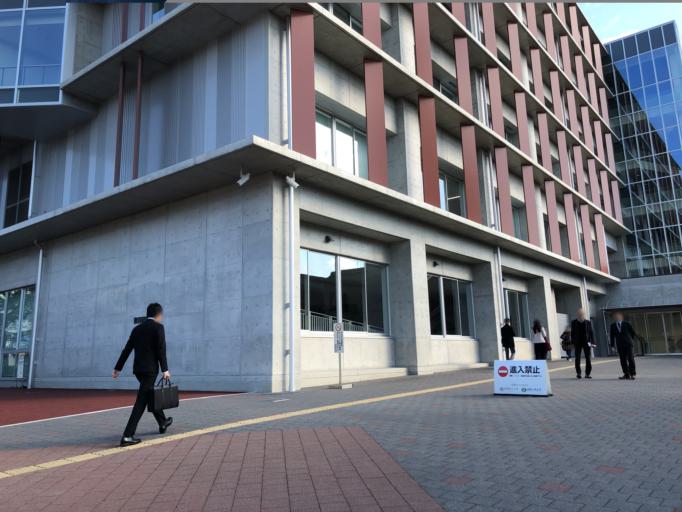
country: JP
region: Kochi
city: Kochi-shi
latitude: 33.5641
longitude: 133.5350
